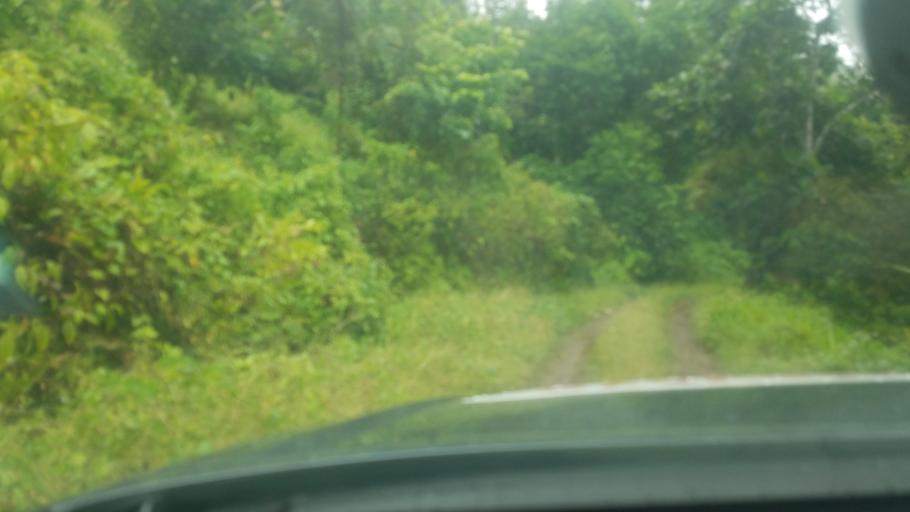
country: LC
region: Gros-Islet
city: Gros Islet
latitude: 14.0347
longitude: -60.9315
